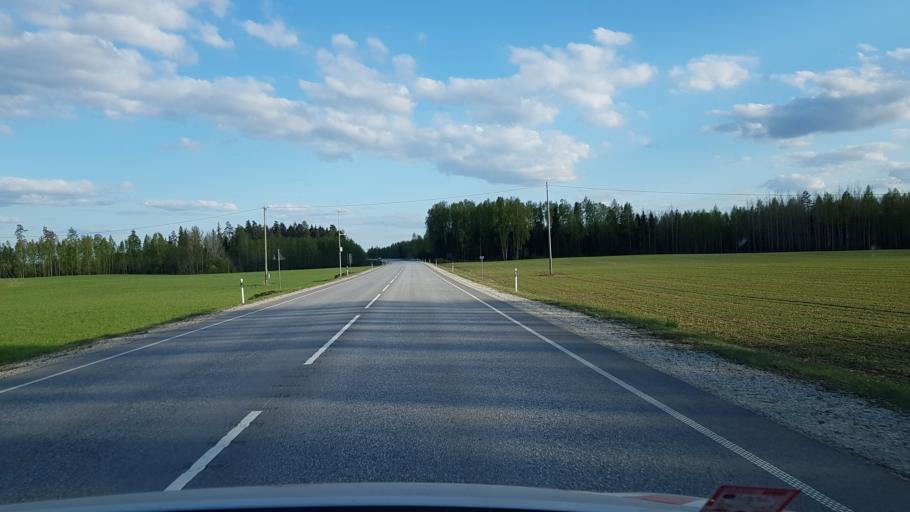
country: EE
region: Vorumaa
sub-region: Voru linn
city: Voru
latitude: 57.9329
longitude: 26.7984
